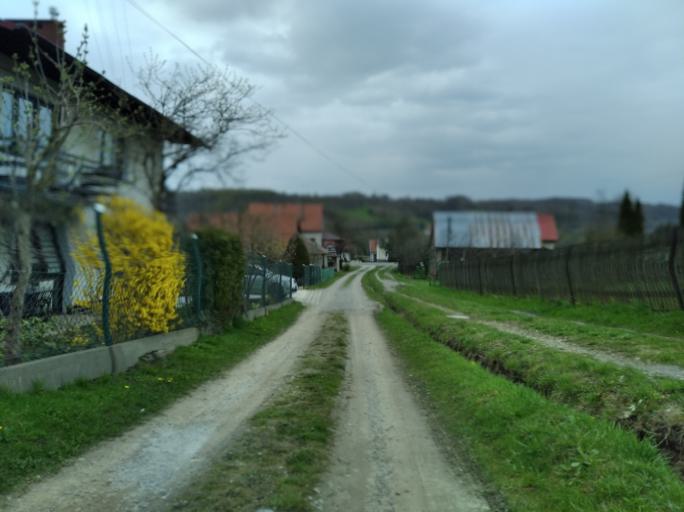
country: PL
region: Subcarpathian Voivodeship
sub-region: Powiat strzyzowski
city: Strzyzow
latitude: 49.8517
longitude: 21.7980
